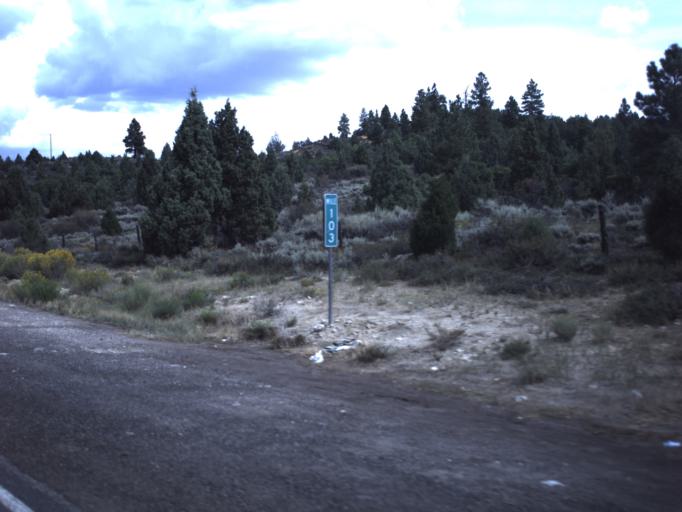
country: US
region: Utah
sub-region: Garfield County
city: Panguitch
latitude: 37.4788
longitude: -112.5140
